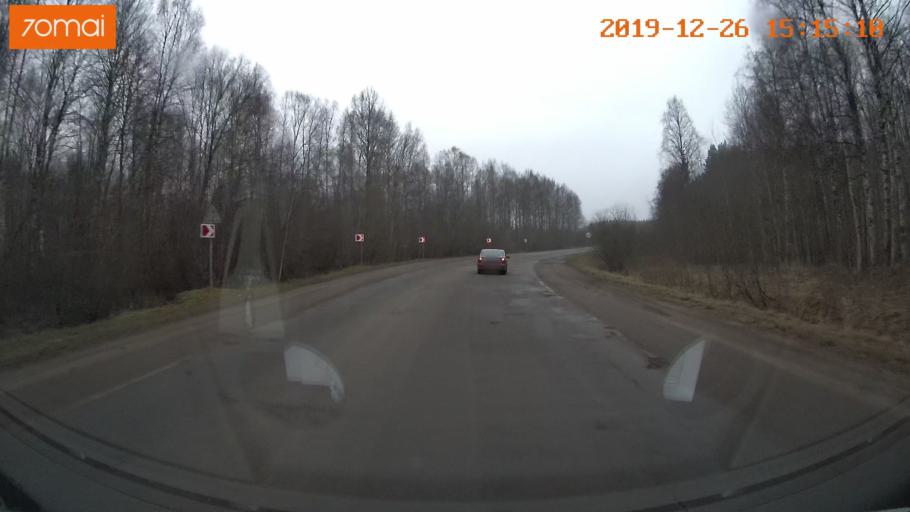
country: RU
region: Jaroslavl
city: Rybinsk
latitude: 58.0993
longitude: 38.8765
